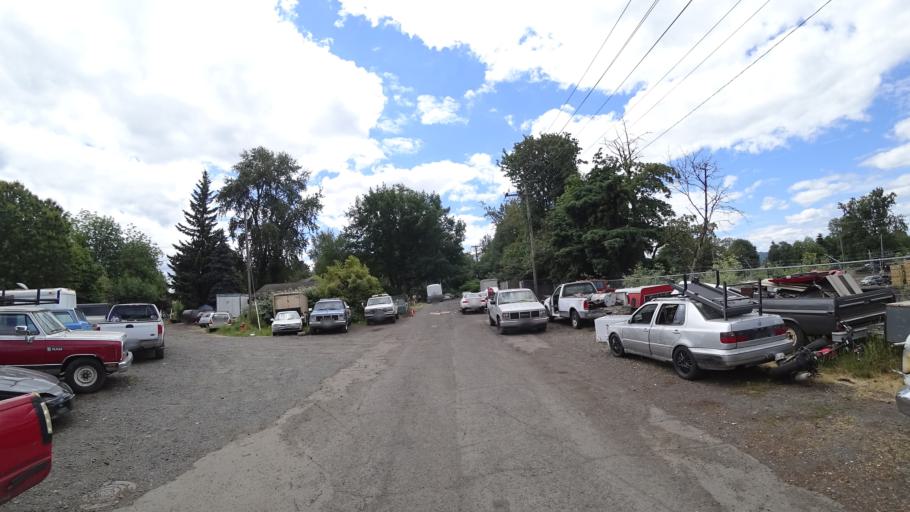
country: US
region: Washington
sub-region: Clark County
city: Vancouver
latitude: 45.5951
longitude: -122.7242
